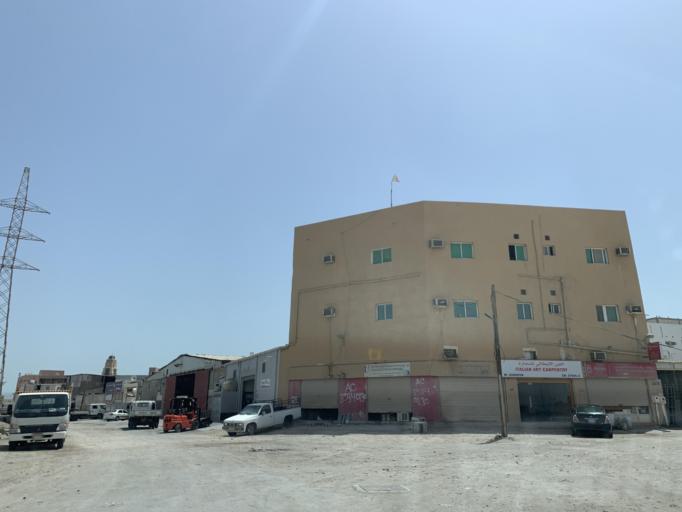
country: BH
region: Northern
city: Sitrah
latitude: 26.1398
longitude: 50.6100
